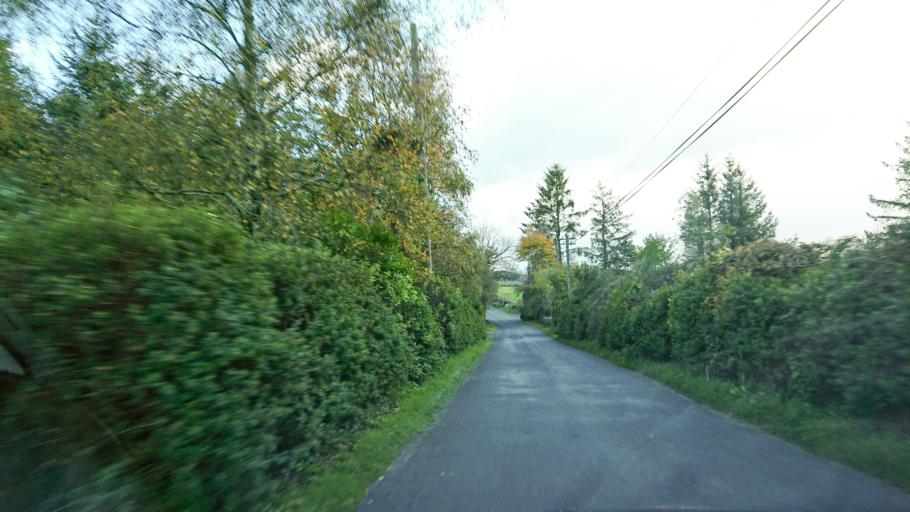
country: IE
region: Leinster
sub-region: Kilkenny
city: Graiguenamanagh
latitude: 52.4804
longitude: -6.9171
